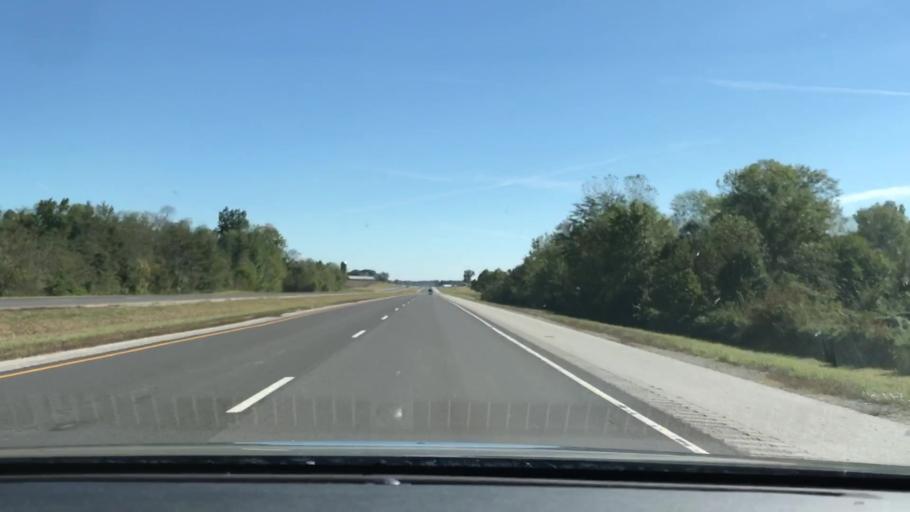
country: US
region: Kentucky
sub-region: Todd County
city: Elkton
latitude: 36.8037
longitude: -87.0775
